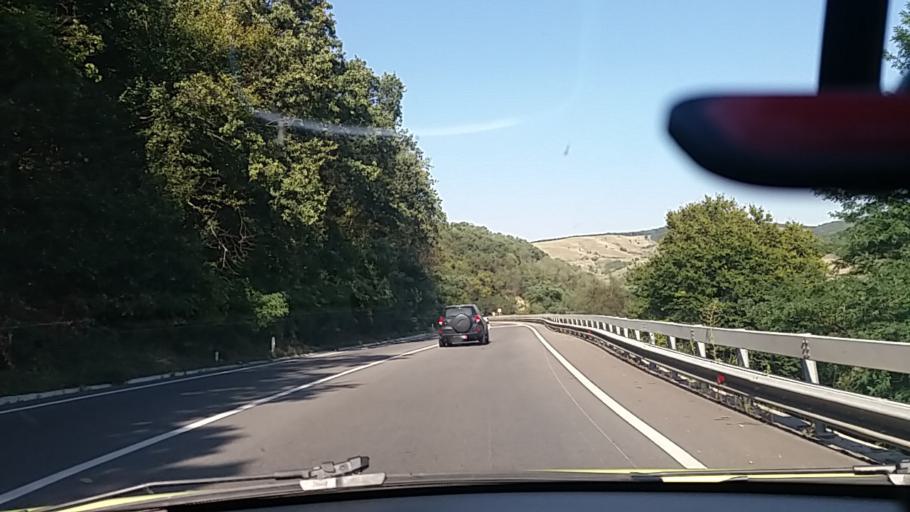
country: RO
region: Sibiu
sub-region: Comuna Slimnic
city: Slimnic
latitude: 45.9427
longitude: 24.1711
